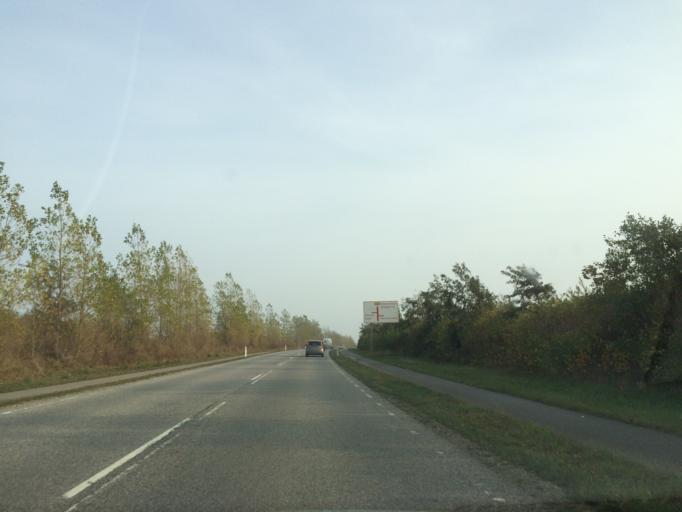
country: DK
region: Zealand
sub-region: Odsherred Kommune
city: Asnaes
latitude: 55.9754
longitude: 11.3405
